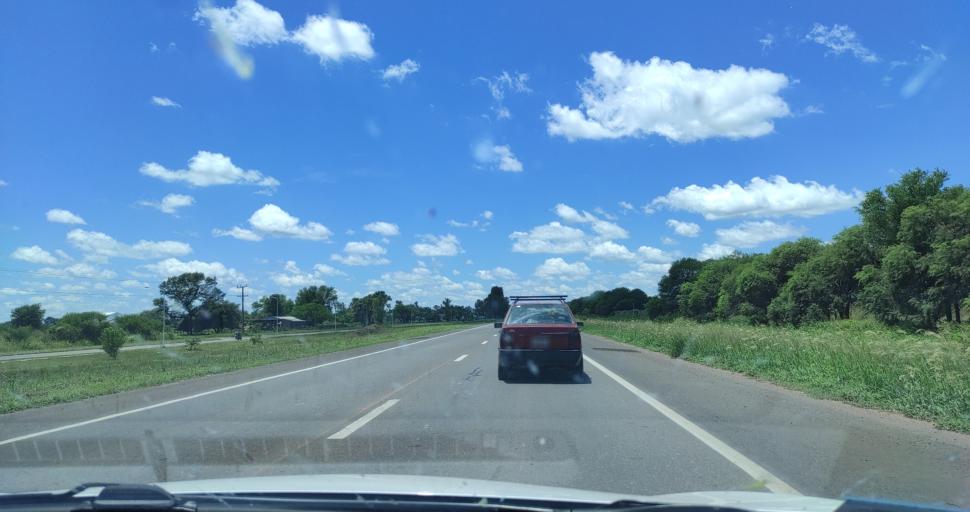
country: AR
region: Chaco
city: Avia Terai
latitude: -26.7029
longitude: -60.7365
